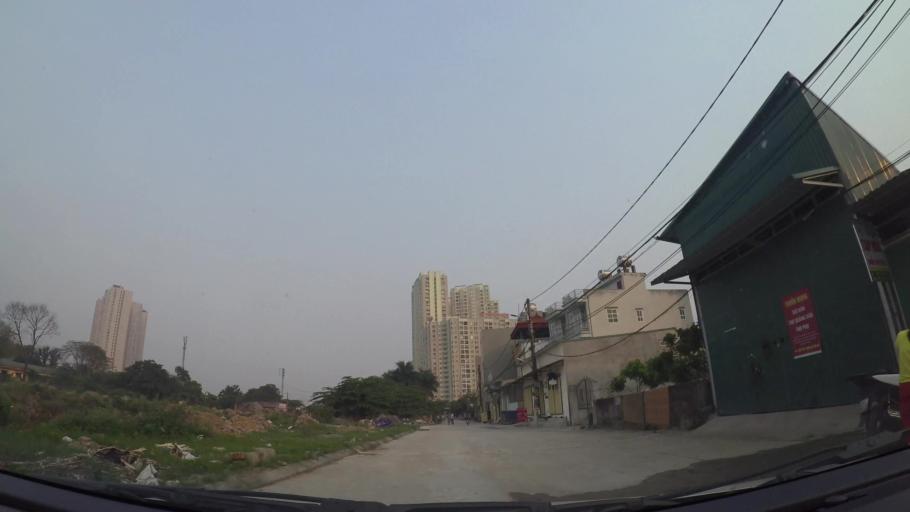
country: VN
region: Ha Noi
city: Cau Dien
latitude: 21.0078
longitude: 105.7248
